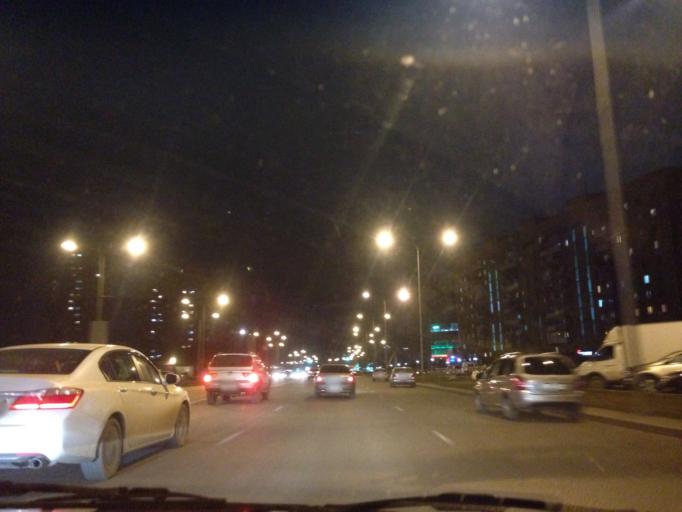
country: KZ
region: Astana Qalasy
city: Astana
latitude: 51.1702
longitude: 71.3869
